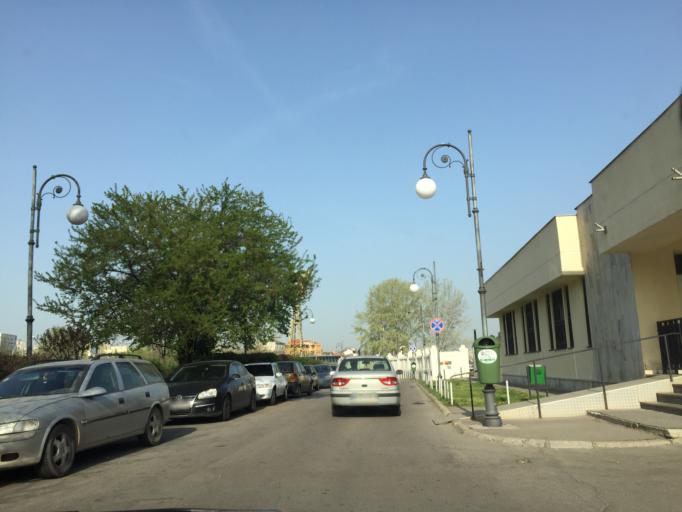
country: RO
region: Bucuresti
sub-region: Municipiul Bucuresti
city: Bucuresti
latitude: 44.4266
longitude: 26.0768
